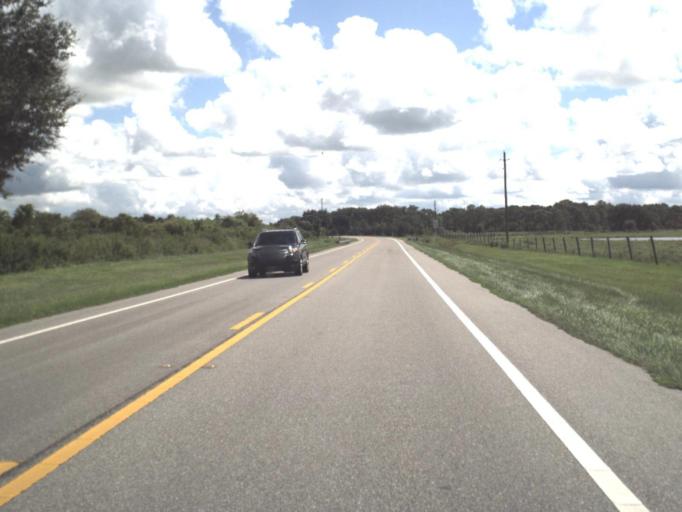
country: US
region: Florida
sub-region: Sarasota County
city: Lake Sarasota
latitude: 27.3647
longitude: -82.2054
